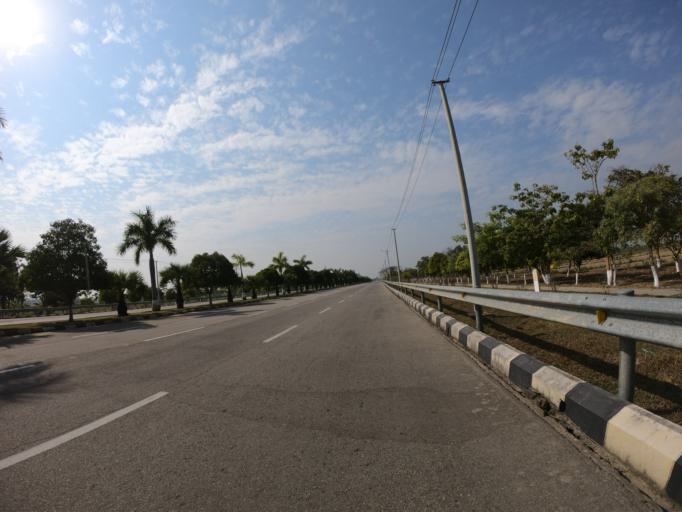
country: MM
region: Mandalay
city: Nay Pyi Taw
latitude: 19.6553
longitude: 96.1337
